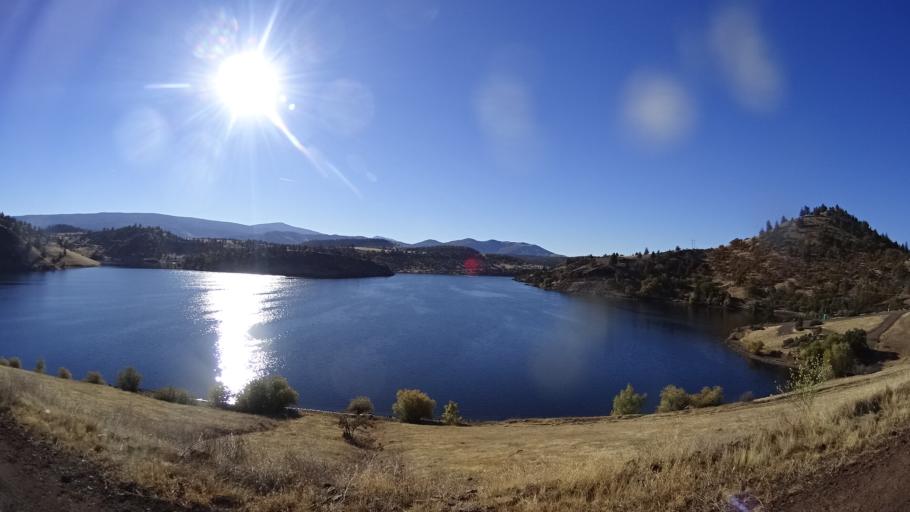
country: US
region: California
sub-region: Siskiyou County
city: Montague
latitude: 41.9481
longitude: -122.4365
